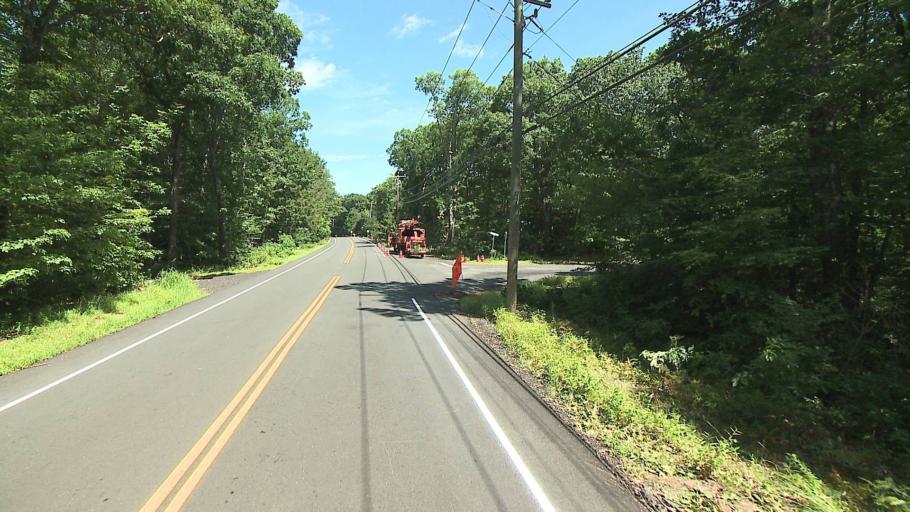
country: US
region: Connecticut
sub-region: Litchfield County
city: New Hartford Center
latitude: 41.9523
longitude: -72.9154
